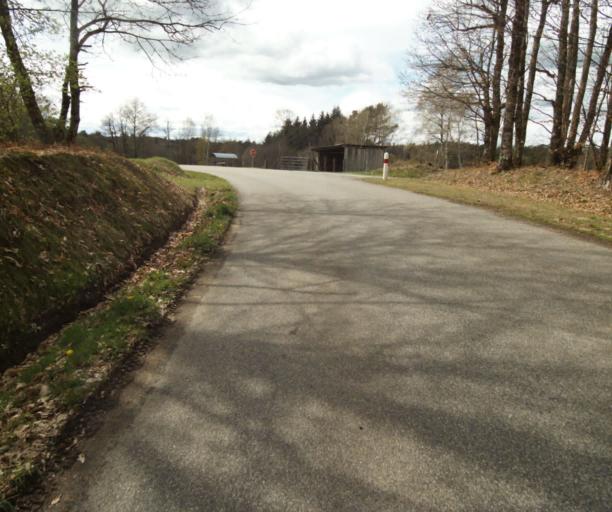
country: FR
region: Limousin
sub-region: Departement de la Correze
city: Laguenne
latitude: 45.2151
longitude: 1.8929
